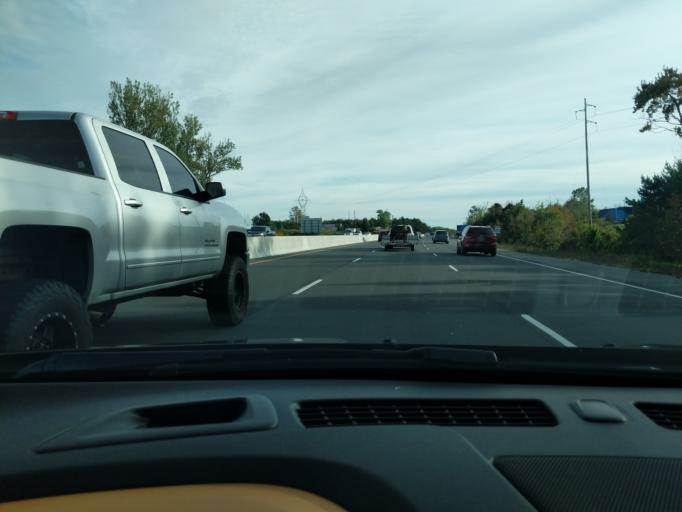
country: CA
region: Ontario
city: Innisfil
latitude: 44.3277
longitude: -79.6830
